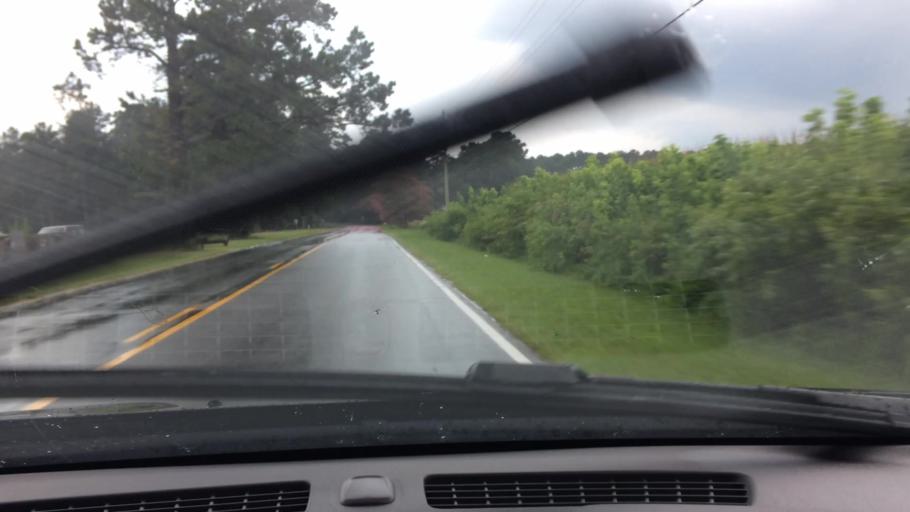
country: US
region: North Carolina
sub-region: Pitt County
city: Winterville
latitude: 35.5075
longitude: -77.3812
